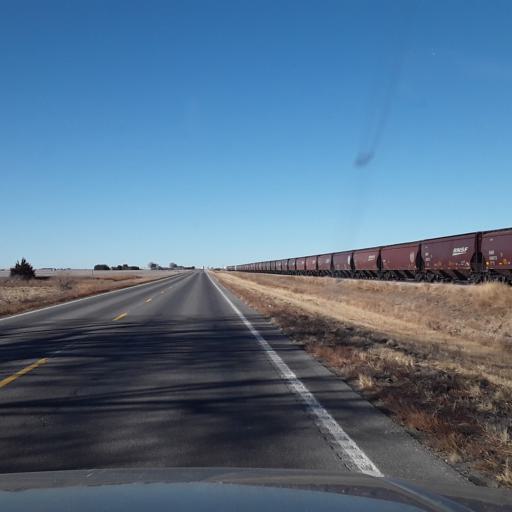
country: US
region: Nebraska
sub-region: Phelps County
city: Holdrege
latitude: 40.4448
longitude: -99.4202
